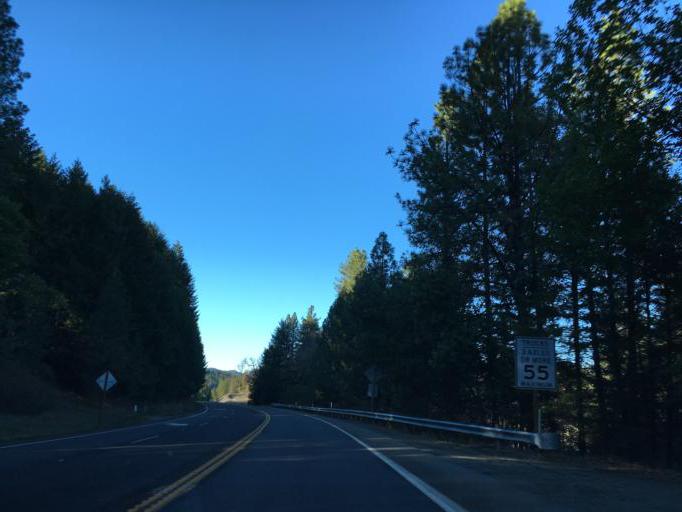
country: US
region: California
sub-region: Mendocino County
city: Laytonville
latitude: 39.7109
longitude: -123.4920
